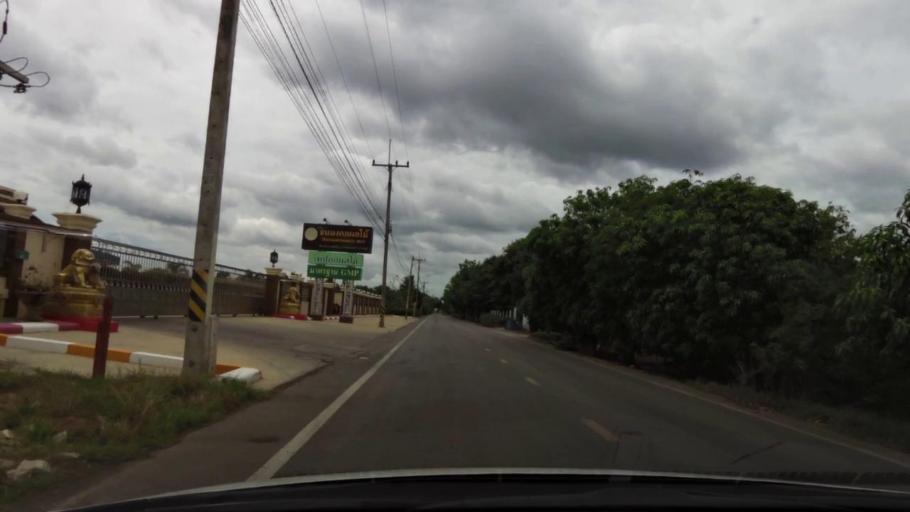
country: TH
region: Ratchaburi
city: Damnoen Saduak
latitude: 13.5517
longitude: 100.0171
